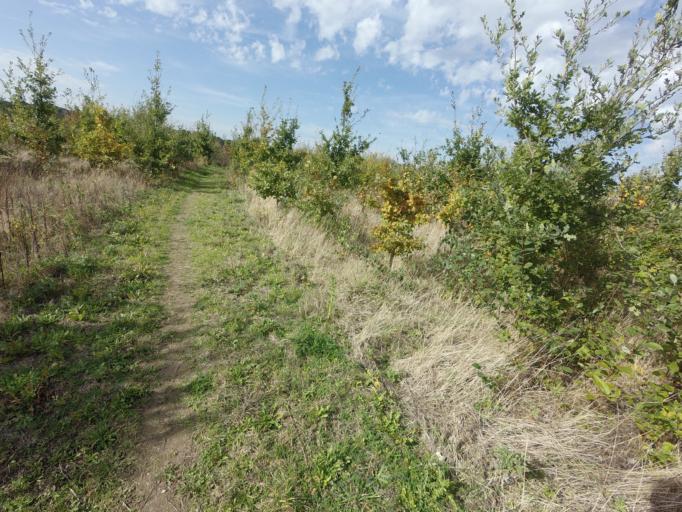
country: NL
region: Limburg
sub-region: Gemeente Kerkrade
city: Kerkrade
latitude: 50.9009
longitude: 6.0531
